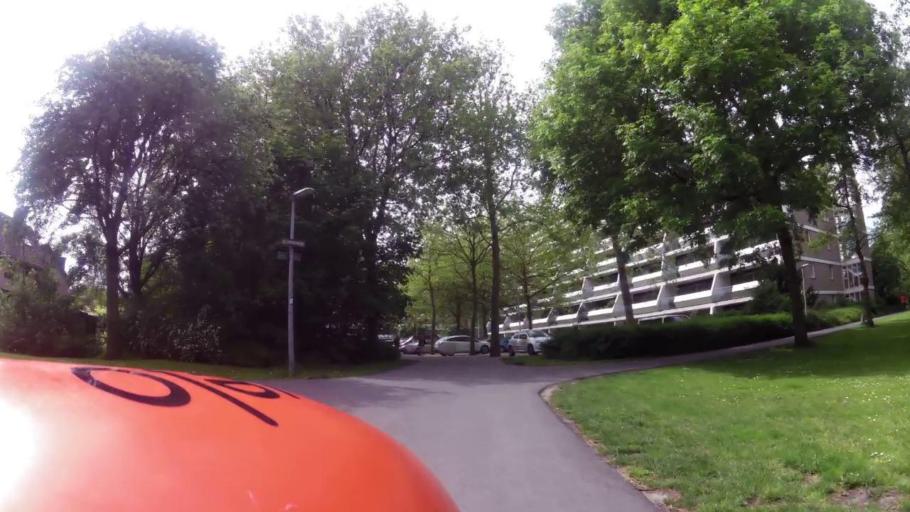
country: NL
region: South Holland
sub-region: Gemeente Leiden
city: Leiden
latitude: 52.1767
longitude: 4.5096
